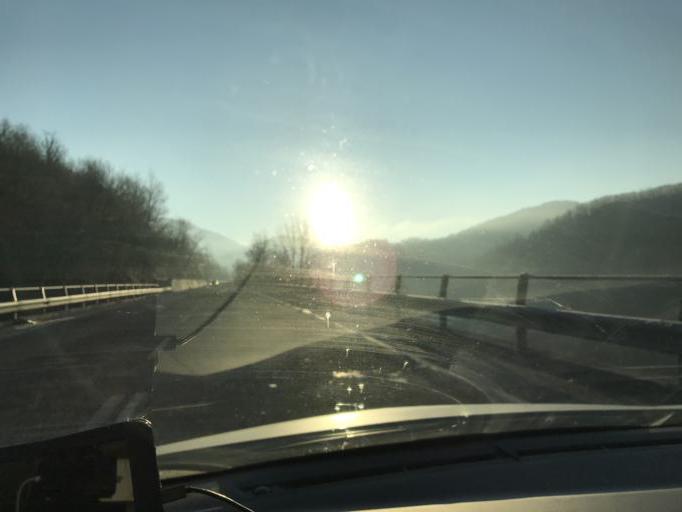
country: IT
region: Latium
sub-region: Provincia di Rieti
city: Concerviano
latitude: 42.3350
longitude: 13.0039
